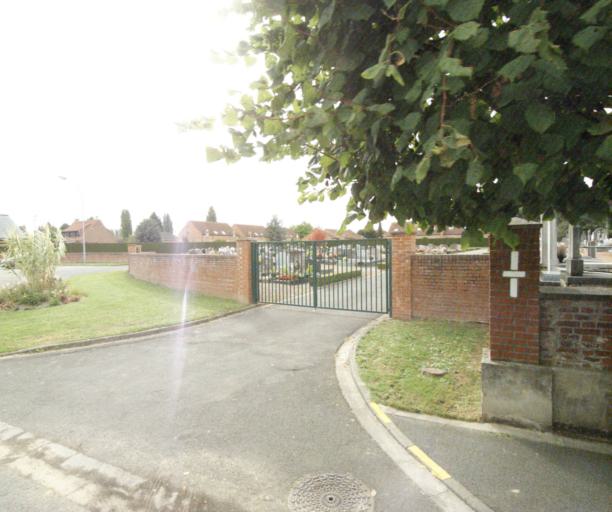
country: FR
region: Nord-Pas-de-Calais
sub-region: Departement du Nord
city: Erquinghem-Lys
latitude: 50.6759
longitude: 2.8497
